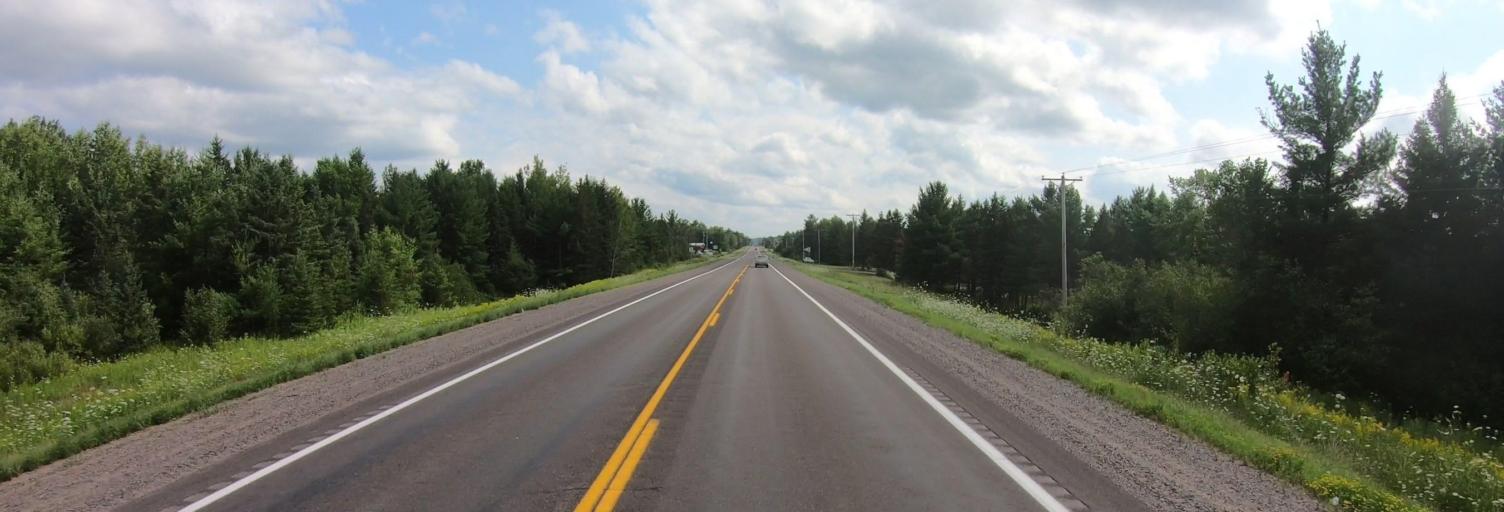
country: US
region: Michigan
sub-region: Ontonagon County
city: Ontonagon
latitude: 46.5519
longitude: -89.1787
